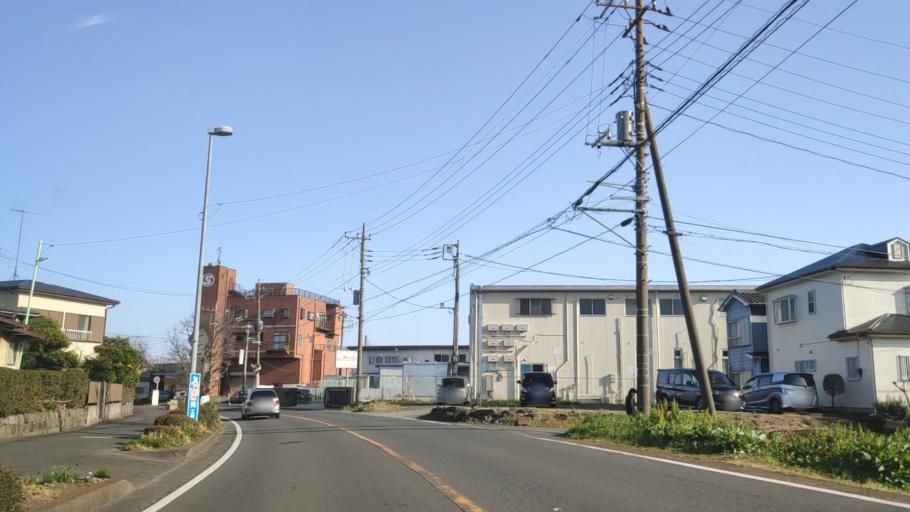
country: JP
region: Kanagawa
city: Zama
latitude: 35.5054
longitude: 139.3409
